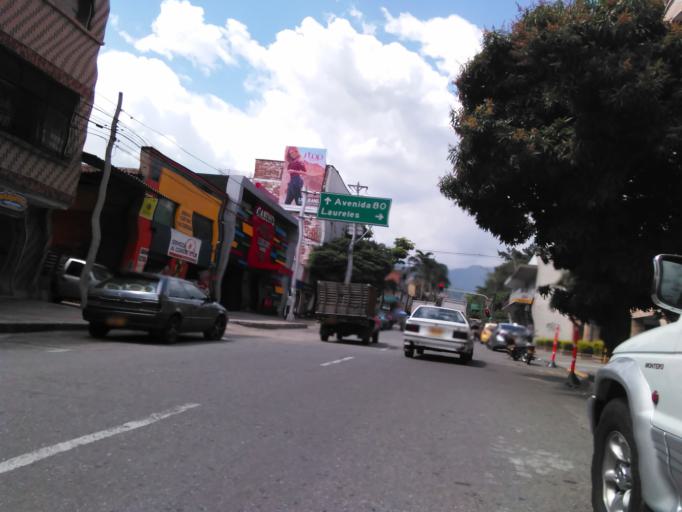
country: CO
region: Antioquia
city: Medellin
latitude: 6.2321
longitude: -75.5955
